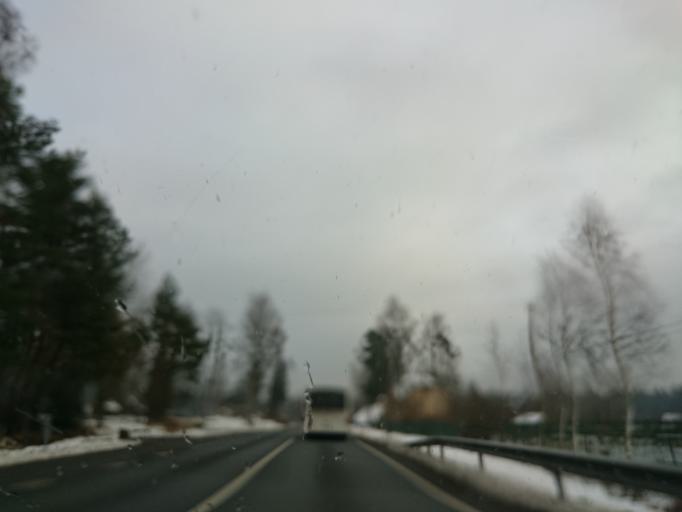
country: LV
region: Ligatne
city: Ligatne
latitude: 57.2933
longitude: 24.9204
